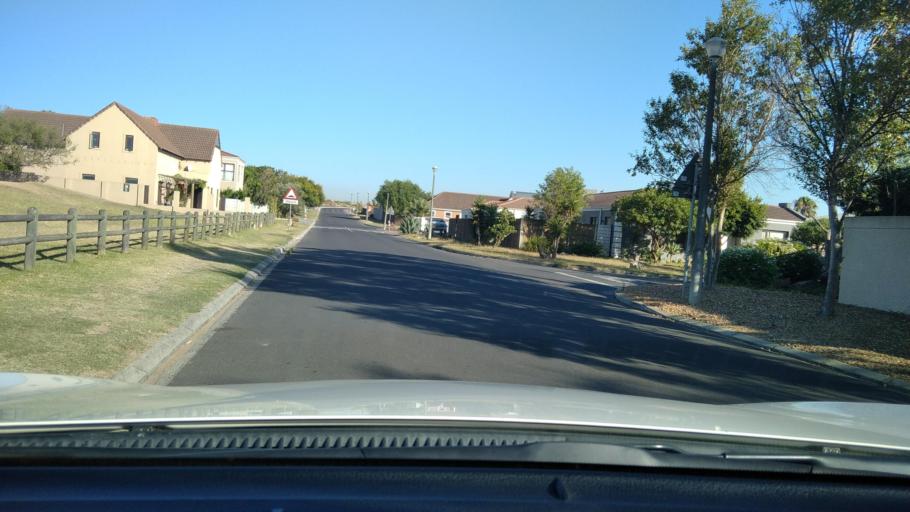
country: ZA
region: Western Cape
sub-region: City of Cape Town
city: Kraaifontein
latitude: -33.8149
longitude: 18.6910
